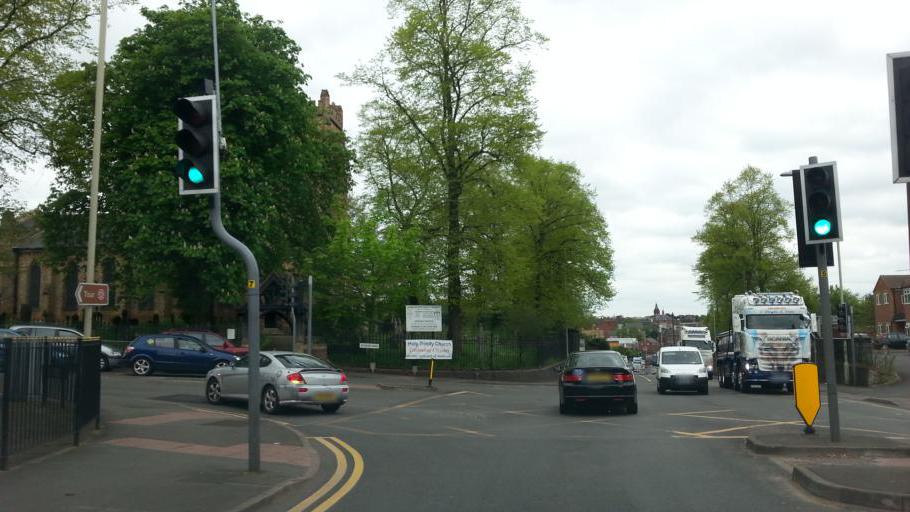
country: GB
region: England
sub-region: Dudley
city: Stourbridge
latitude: 52.4635
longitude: -2.1498
